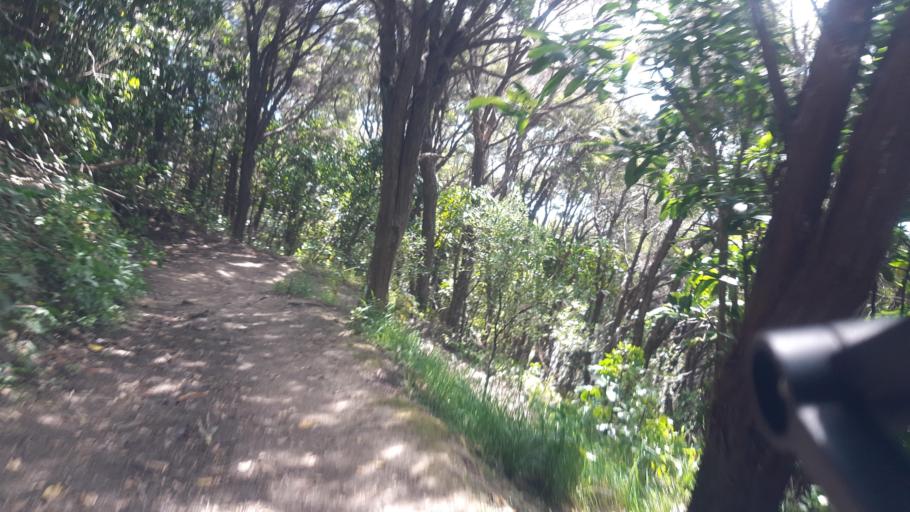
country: NZ
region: Marlborough
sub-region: Marlborough District
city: Picton
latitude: -41.2591
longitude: 174.0361
